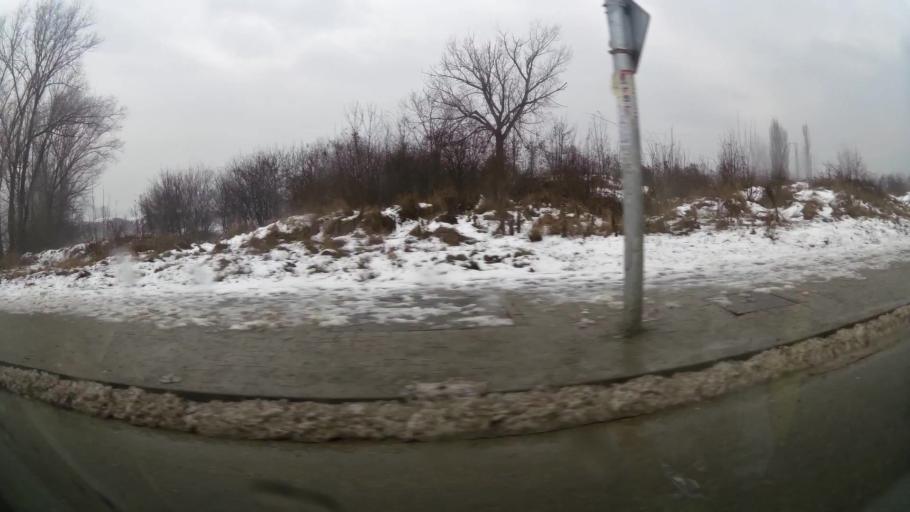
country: BG
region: Sofia-Capital
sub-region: Stolichna Obshtina
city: Sofia
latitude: 42.6825
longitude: 23.2556
